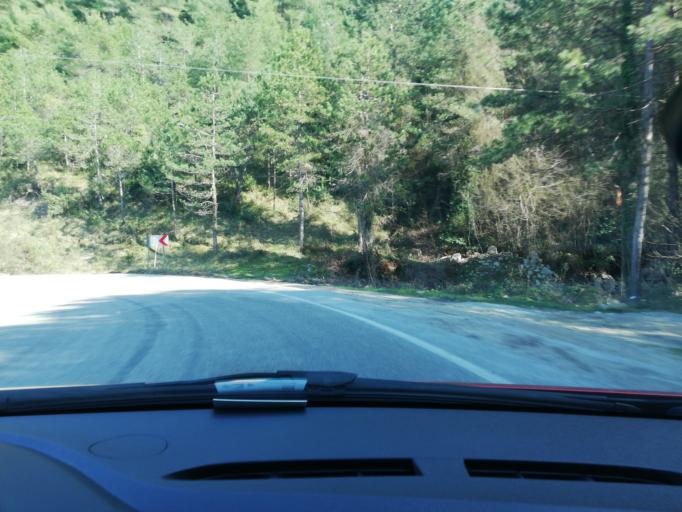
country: TR
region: Bartin
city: Kurucasile
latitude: 41.8358
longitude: 32.7088
